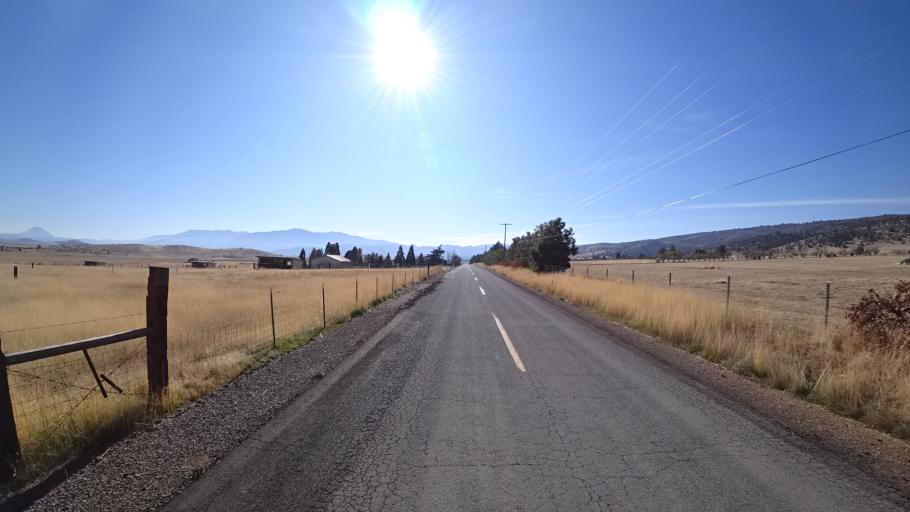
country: US
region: California
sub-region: Siskiyou County
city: Montague
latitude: 41.5951
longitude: -122.5405
